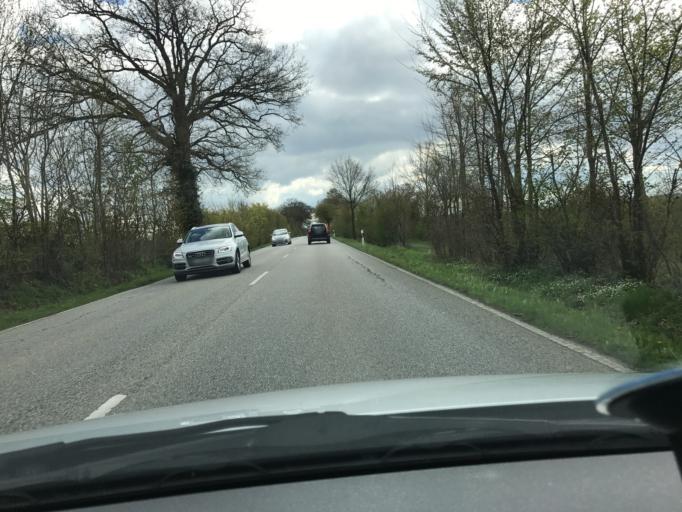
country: DE
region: Schleswig-Holstein
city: Dornick
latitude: 54.1811
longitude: 10.3758
